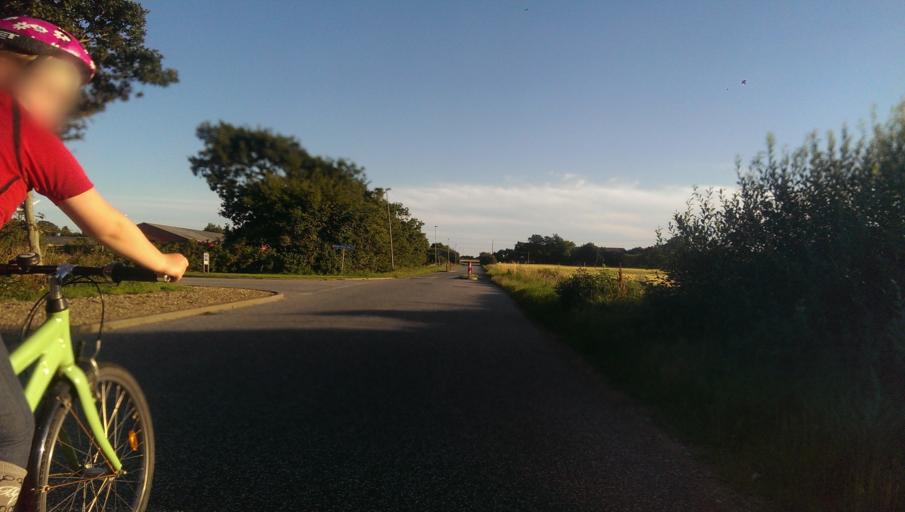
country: DK
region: South Denmark
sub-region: Esbjerg Kommune
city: Tjaereborg
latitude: 55.4593
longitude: 8.5829
